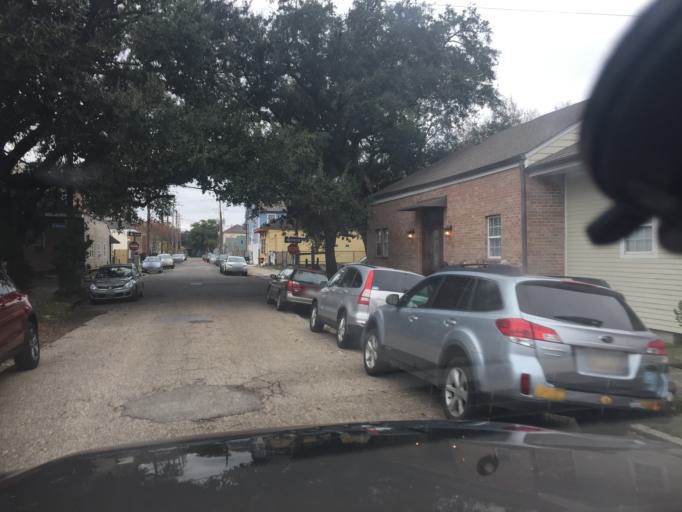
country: US
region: Louisiana
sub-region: Orleans Parish
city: New Orleans
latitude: 29.9765
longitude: -90.0751
